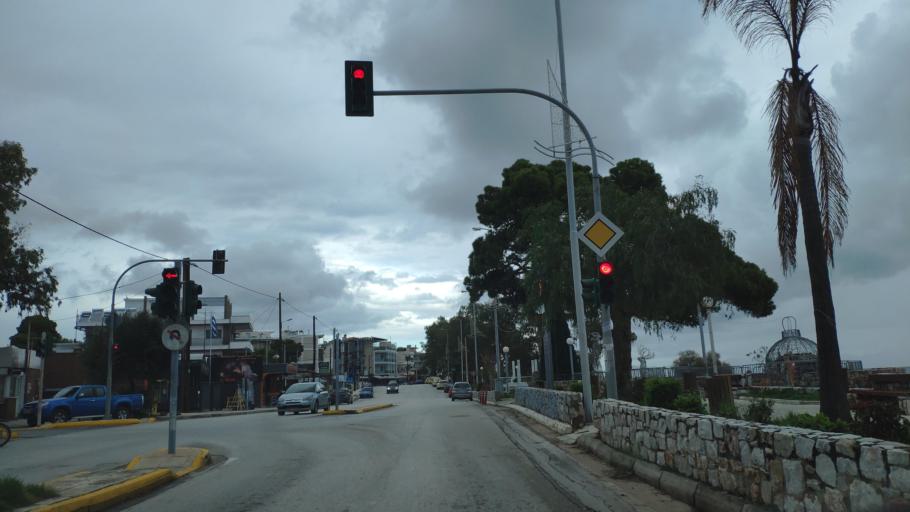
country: GR
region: Attica
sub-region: Nomarchia Anatolikis Attikis
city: Artemida
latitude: 37.9700
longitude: 24.0076
